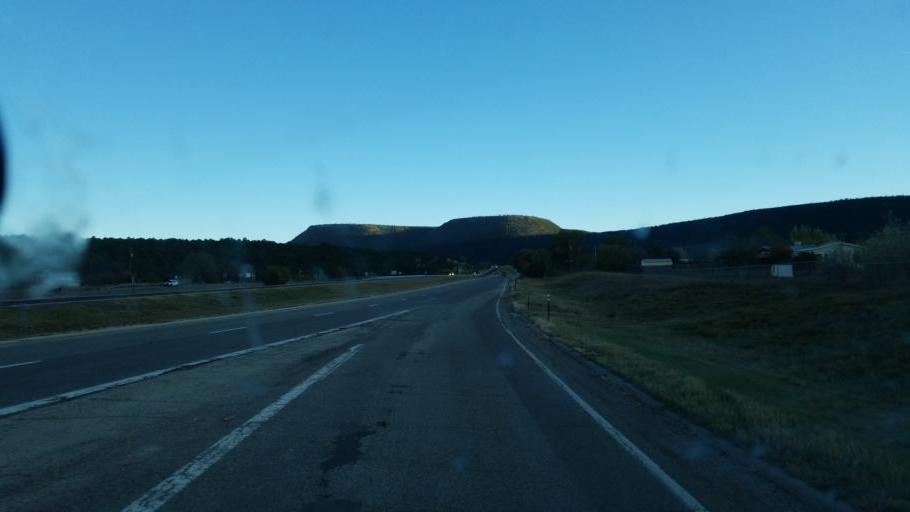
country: US
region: New Mexico
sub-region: San Miguel County
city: Pecos
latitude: 35.4935
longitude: -105.6730
